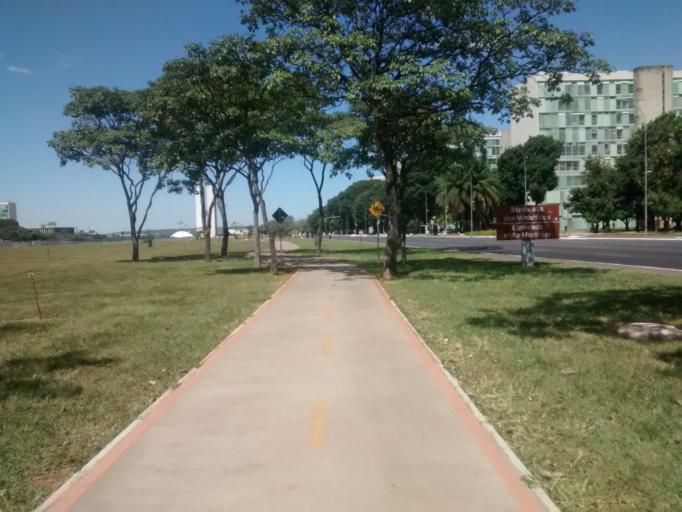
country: BR
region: Federal District
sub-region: Brasilia
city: Brasilia
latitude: -15.7975
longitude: -47.8737
